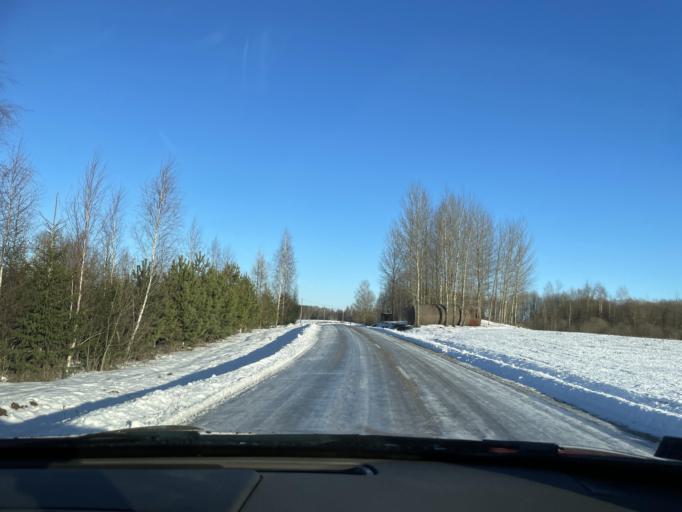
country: LV
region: Ludzas Rajons
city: Ludza
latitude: 56.4590
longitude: 27.5682
